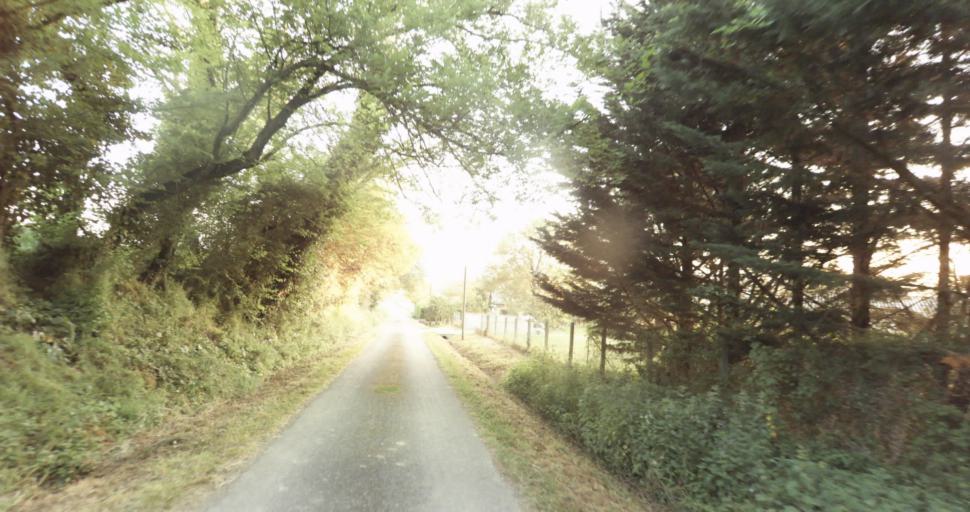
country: FR
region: Midi-Pyrenees
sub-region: Departement du Gers
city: Pujaudran
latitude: 43.6521
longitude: 1.1048
